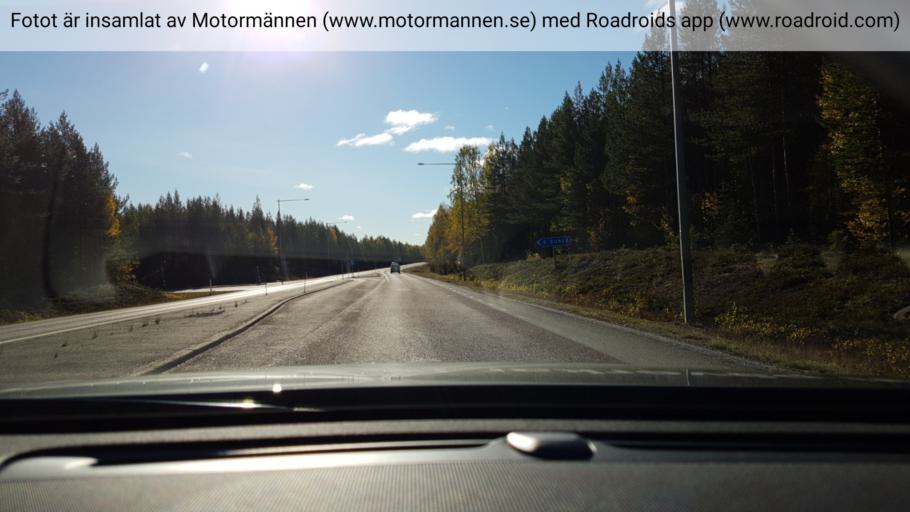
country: SE
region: Vaesterbotten
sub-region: Skelleftea Kommun
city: Burea
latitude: 64.6322
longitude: 21.1750
